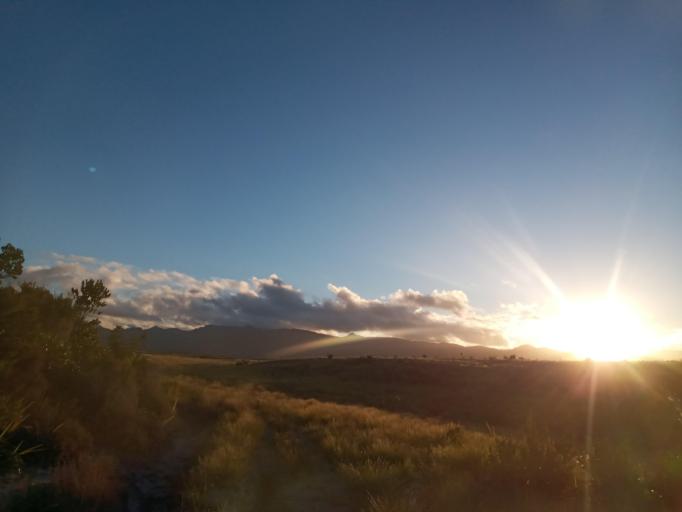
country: MG
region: Anosy
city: Fort Dauphin
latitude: -24.5142
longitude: 47.2489
